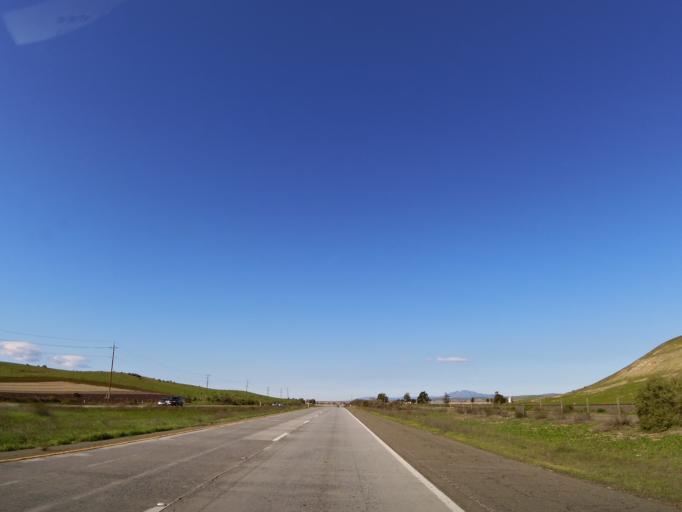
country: US
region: California
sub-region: Monterey County
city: King City
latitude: 36.1616
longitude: -121.0513
